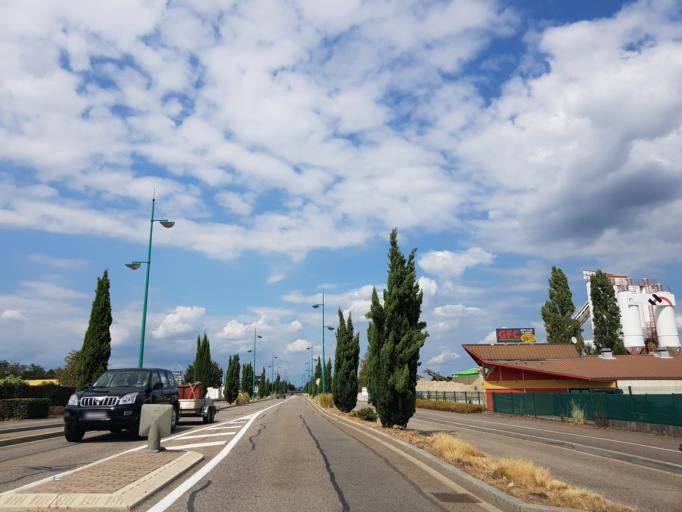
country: FR
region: Alsace
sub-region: Departement du Haut-Rhin
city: Sausheim
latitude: 47.7824
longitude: 7.3887
